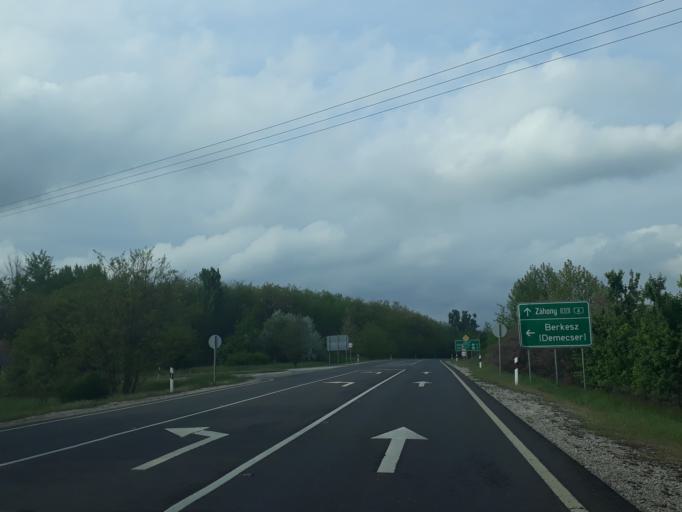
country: HU
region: Szabolcs-Szatmar-Bereg
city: Nyirtass
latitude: 48.1095
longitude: 21.9893
